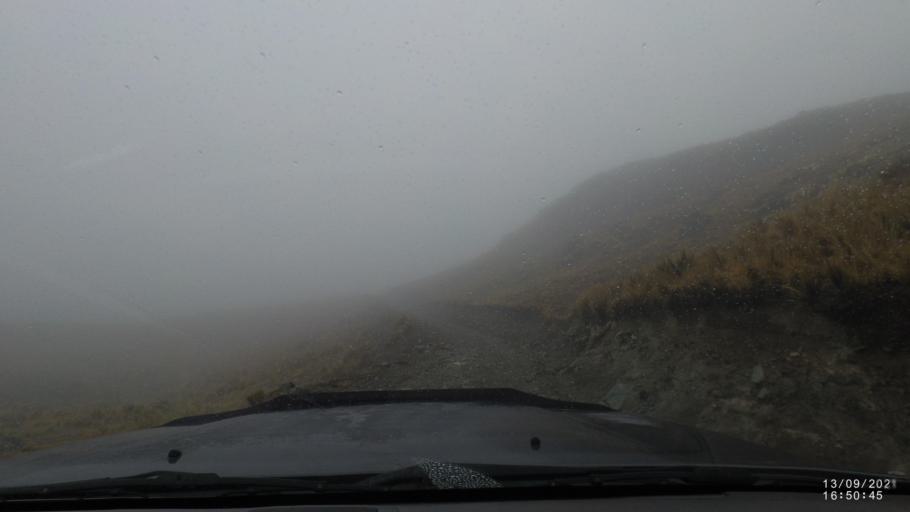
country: BO
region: Cochabamba
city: Colomi
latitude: -17.3054
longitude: -65.7067
